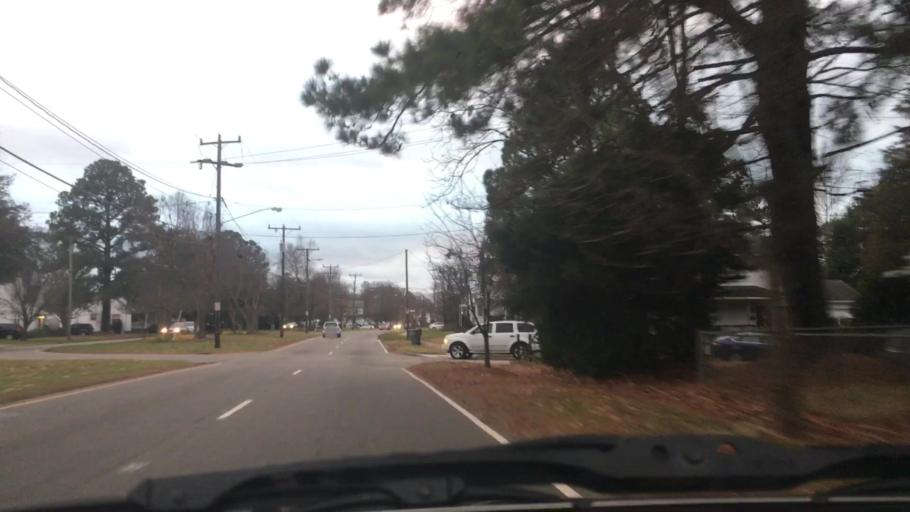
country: US
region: Virginia
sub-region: City of Norfolk
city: Norfolk
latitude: 36.8821
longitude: -76.2472
